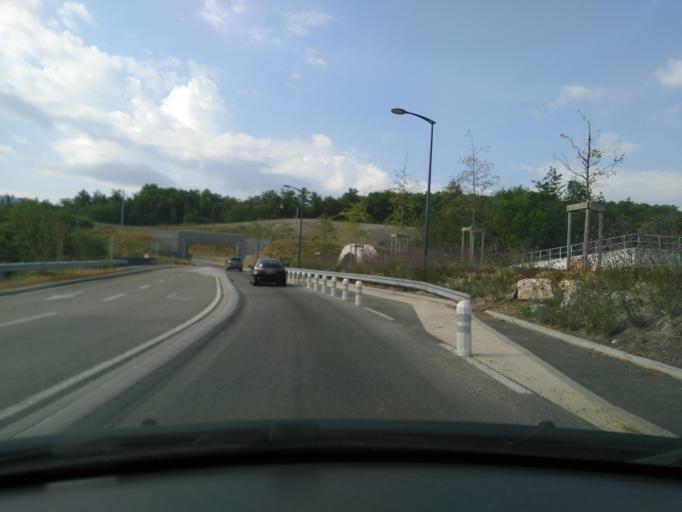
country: FR
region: Rhone-Alpes
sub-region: Departement de la Haute-Savoie
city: Saint-Julien-en-Genevois
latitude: 46.1392
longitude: 6.0734
